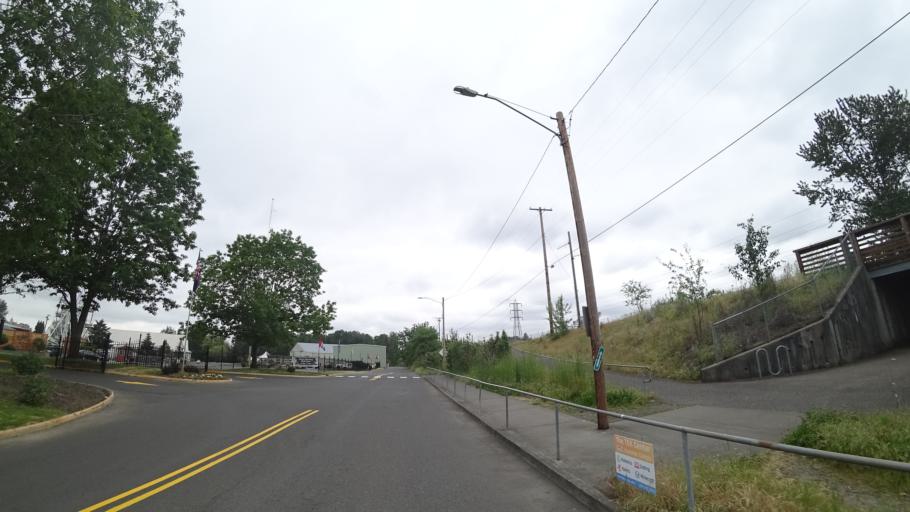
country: US
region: Oregon
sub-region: Clackamas County
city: Milwaukie
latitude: 45.4717
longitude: -122.6614
